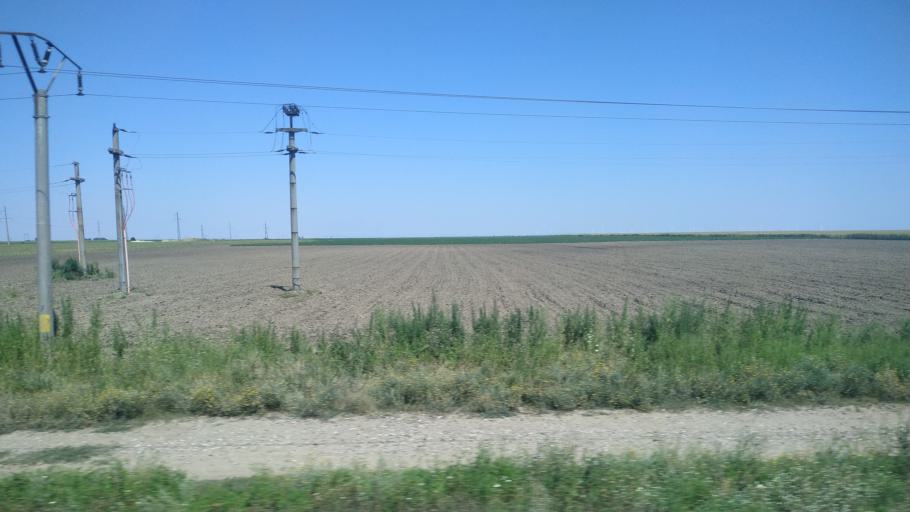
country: RO
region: Calarasi
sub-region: Comuna Borcea
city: Borcea
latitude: 44.4206
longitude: 27.6754
